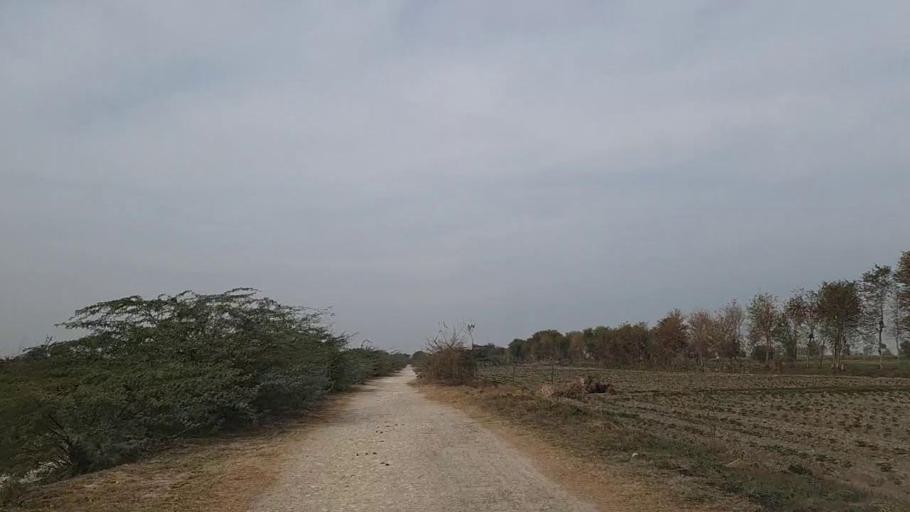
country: PK
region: Sindh
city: Daur
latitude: 26.4209
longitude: 68.4202
